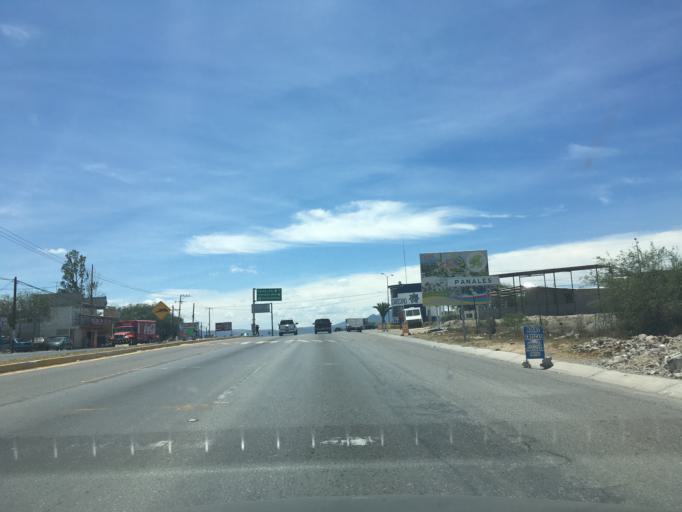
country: MX
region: Hidalgo
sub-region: Ixmiquilpan
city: Panales
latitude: 20.4798
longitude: -99.2612
